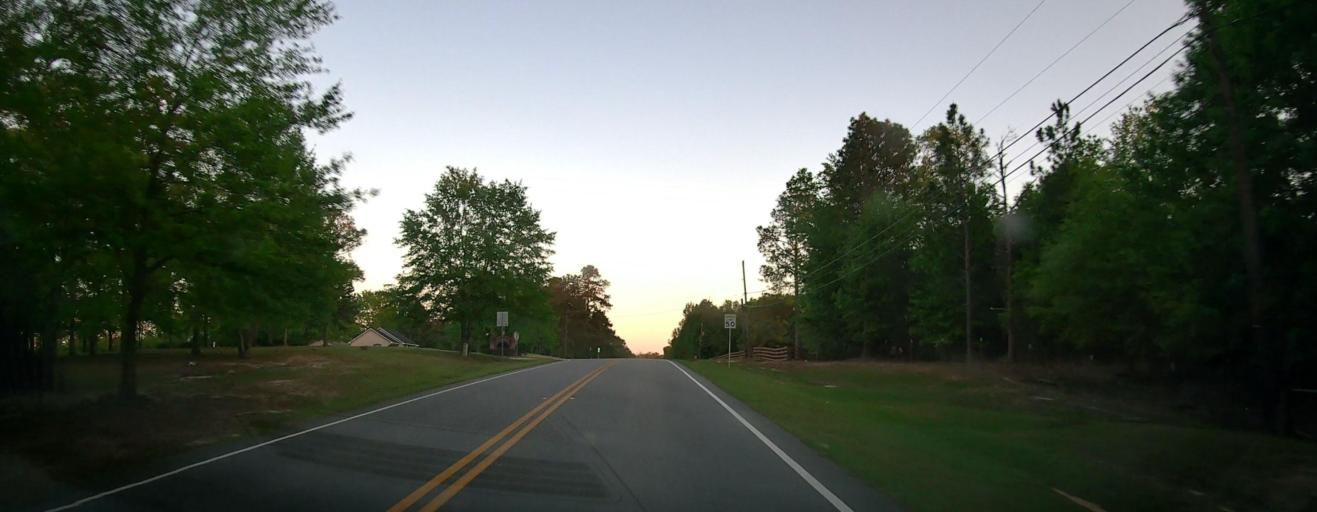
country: US
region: Georgia
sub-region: Marion County
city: Buena Vista
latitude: 32.3389
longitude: -84.5317
